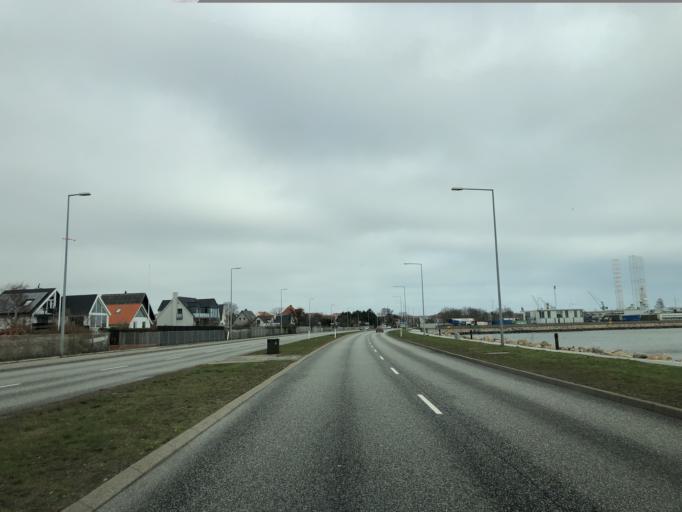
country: DK
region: North Denmark
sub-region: Frederikshavn Kommune
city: Frederikshavn
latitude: 57.4288
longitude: 10.5265
